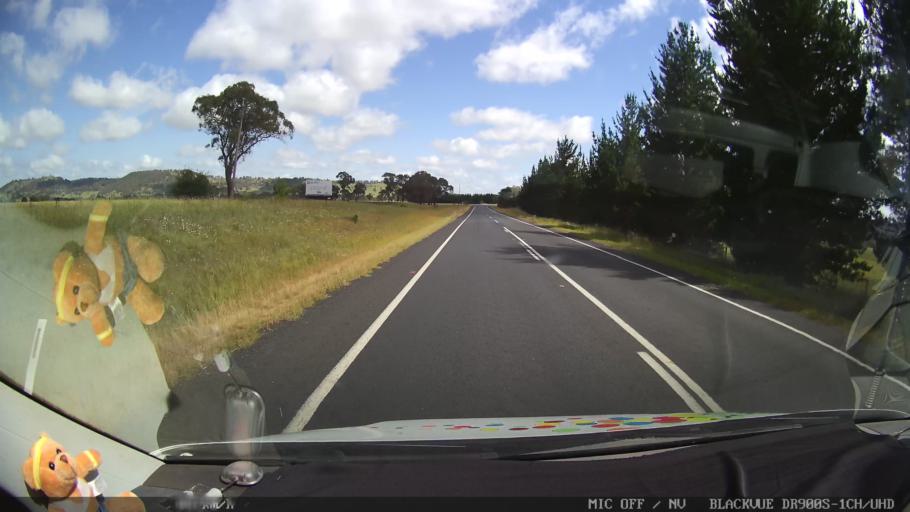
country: AU
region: New South Wales
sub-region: Glen Innes Severn
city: Glen Innes
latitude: -29.8820
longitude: 151.7341
